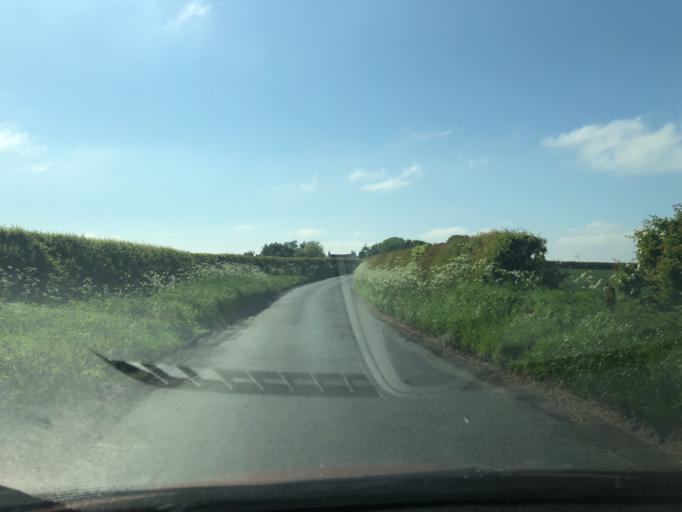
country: GB
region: England
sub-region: North Yorkshire
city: Northallerton
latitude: 54.3310
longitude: -1.4166
